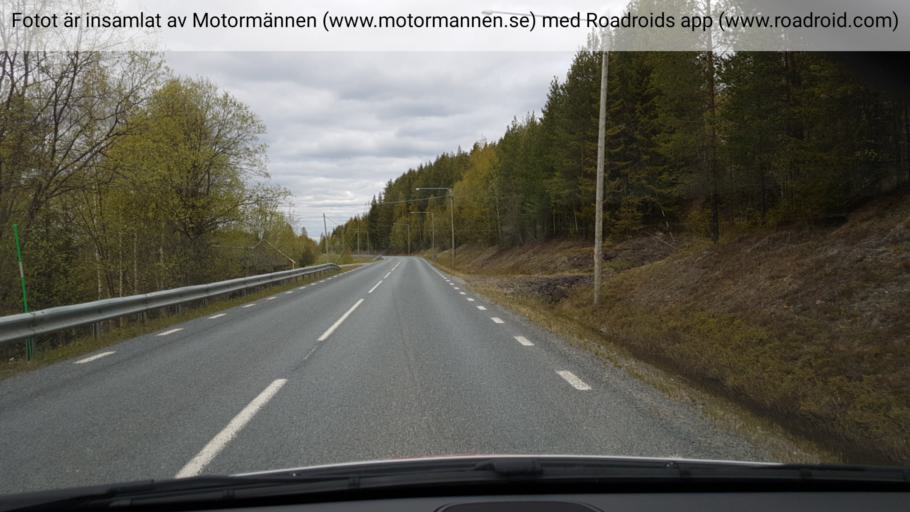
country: SE
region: Vaesterbotten
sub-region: Lycksele Kommun
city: Soderfors
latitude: 65.1030
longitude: 18.3109
